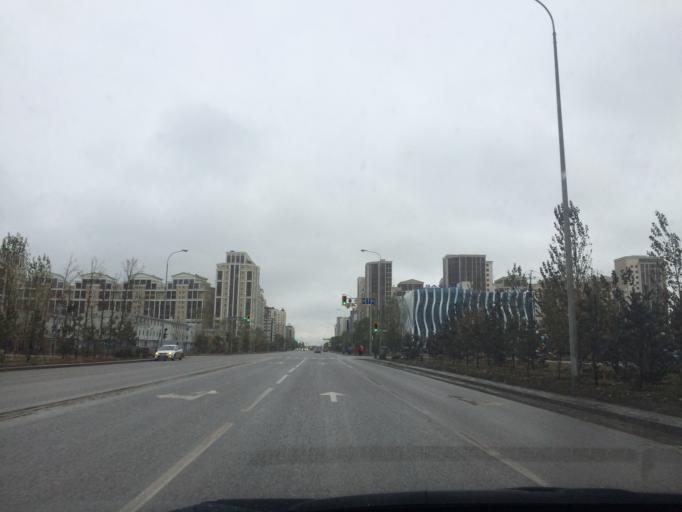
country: KZ
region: Astana Qalasy
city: Astana
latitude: 51.1146
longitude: 71.4218
